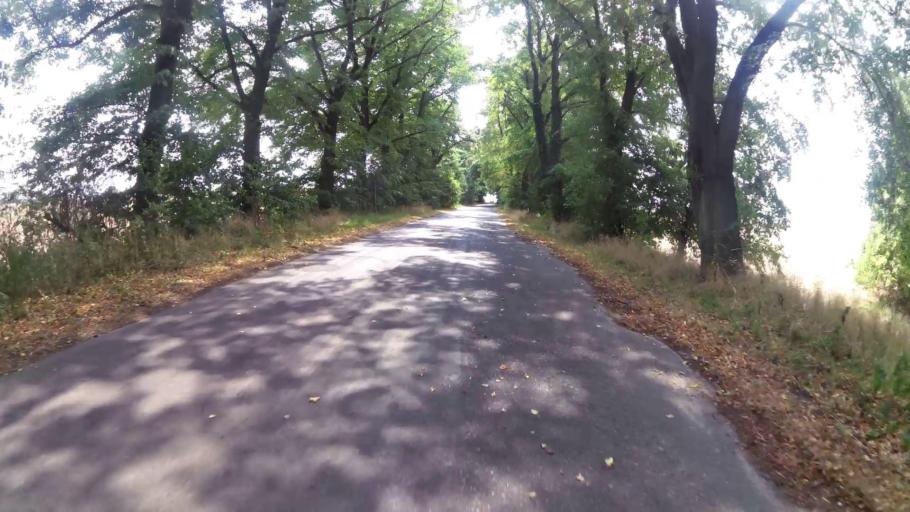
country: PL
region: West Pomeranian Voivodeship
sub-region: Powiat gryfinski
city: Mieszkowice
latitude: 52.8839
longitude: 14.5280
